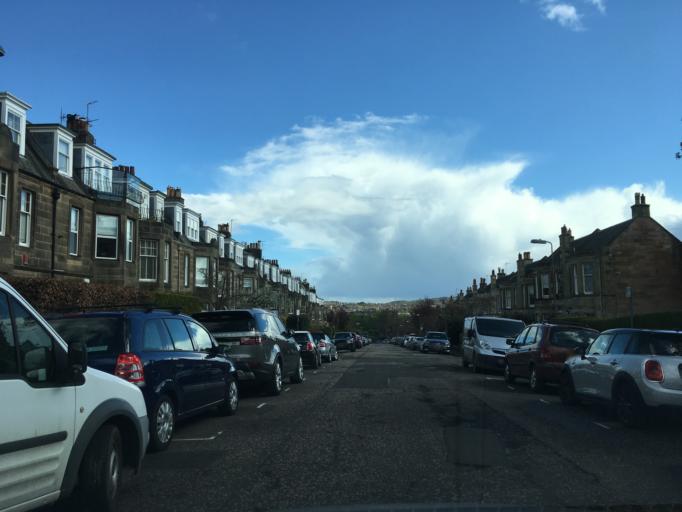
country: GB
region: Scotland
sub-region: Edinburgh
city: Colinton
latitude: 55.9478
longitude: -3.2407
